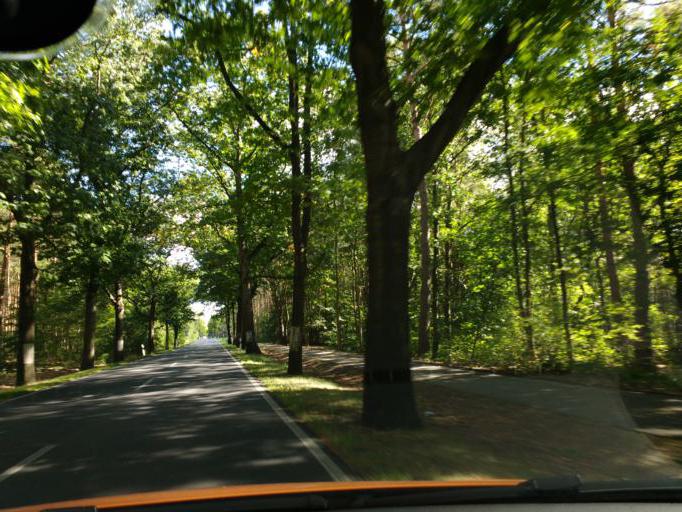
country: DE
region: Brandenburg
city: Bestensee
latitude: 52.2426
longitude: 13.6779
